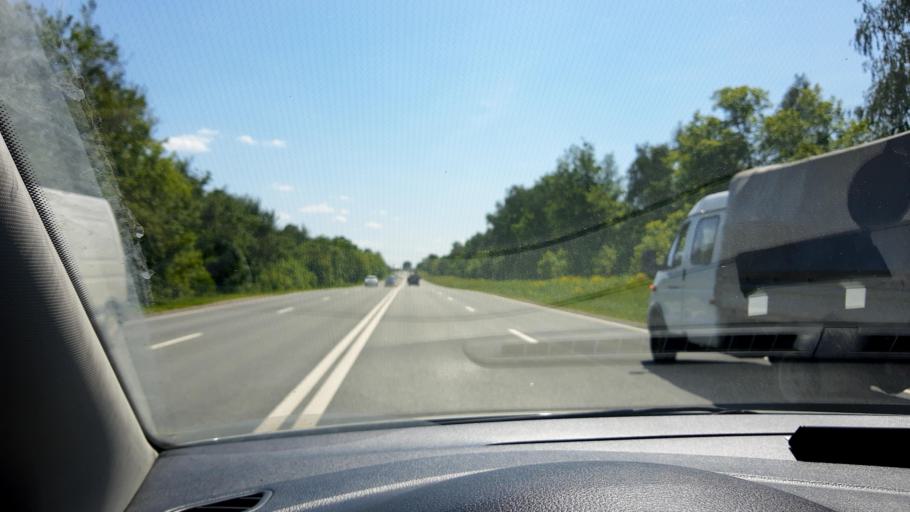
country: RU
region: Moskovskaya
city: Bronnitsy
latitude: 55.4526
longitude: 38.2051
